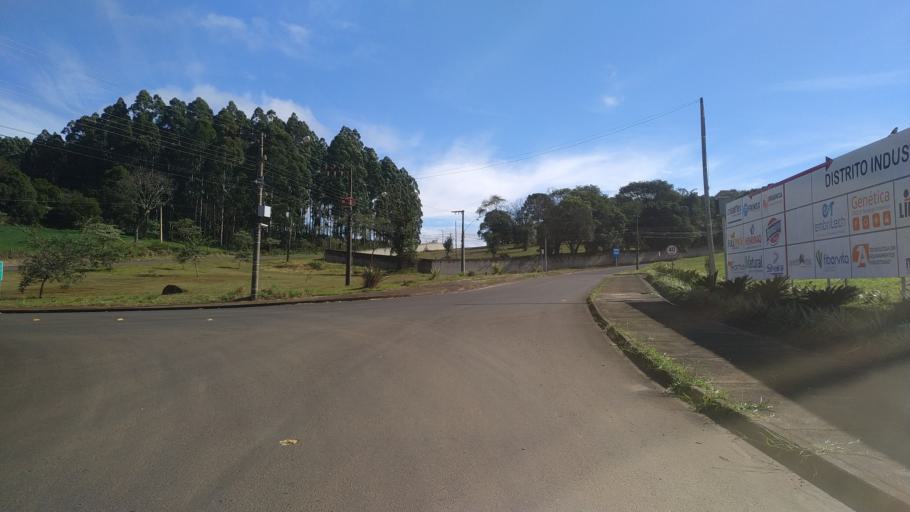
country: BR
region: Santa Catarina
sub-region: Chapeco
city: Chapeco
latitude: -27.1601
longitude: -52.6054
